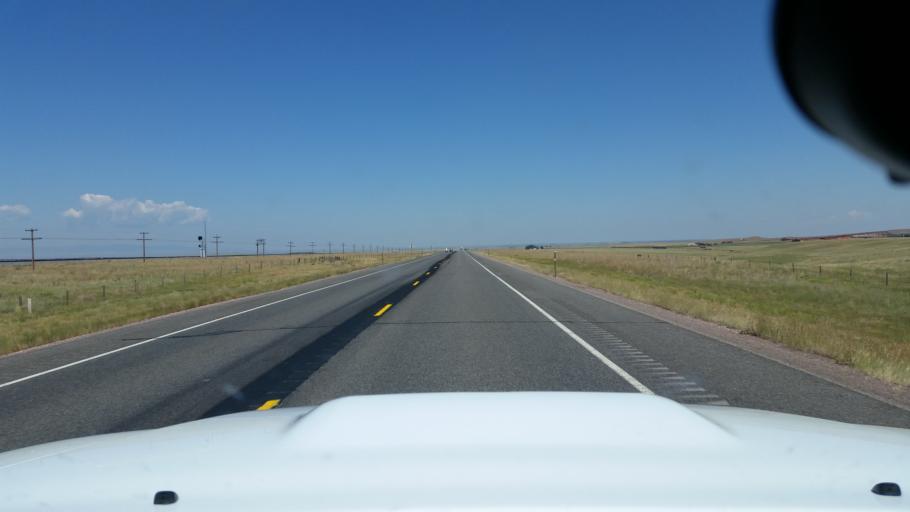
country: US
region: Wyoming
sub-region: Albany County
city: Laramie
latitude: 41.1463
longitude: -105.5657
